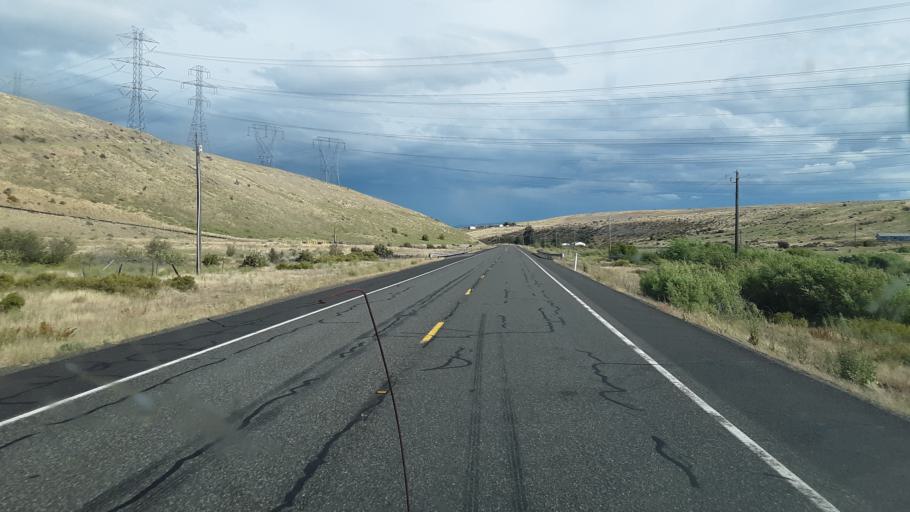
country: US
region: Washington
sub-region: Kittitas County
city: Ellensburg
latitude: 47.1331
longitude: -120.6854
